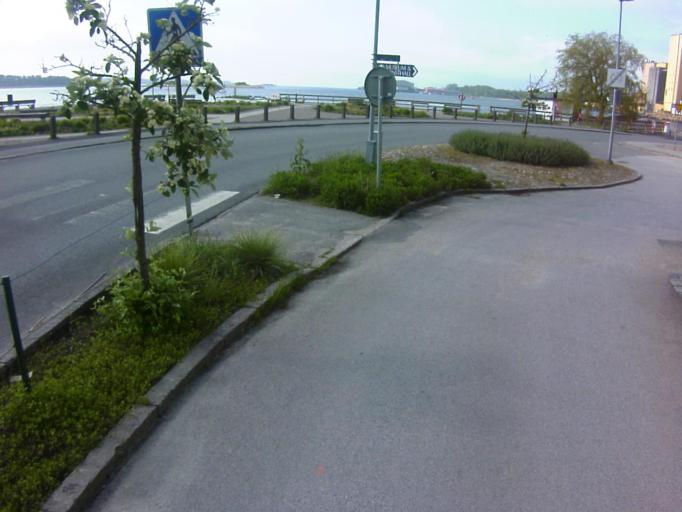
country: SE
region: Blekinge
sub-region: Solvesborgs Kommun
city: Soelvesborg
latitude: 56.0511
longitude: 14.5889
